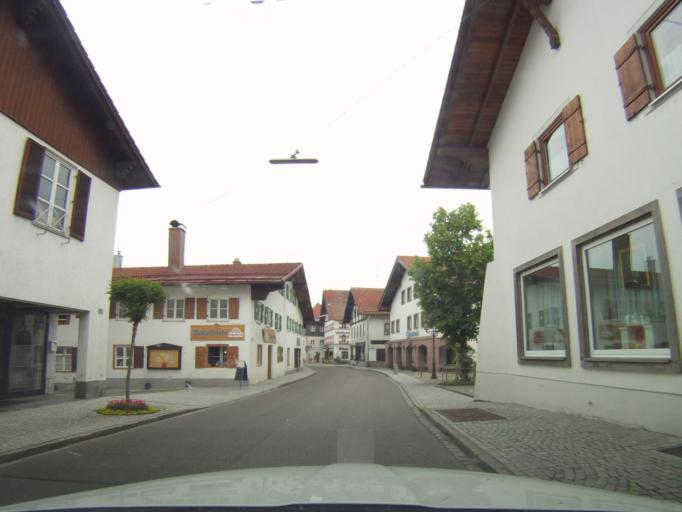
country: DE
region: Bavaria
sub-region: Swabia
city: Nesselwang
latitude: 47.6217
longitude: 10.5002
